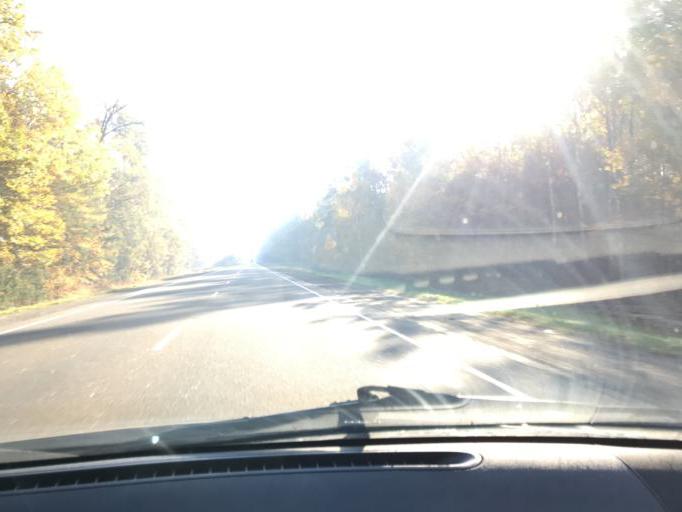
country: BY
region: Brest
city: Horad Luninyets
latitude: 52.2883
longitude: 26.7866
